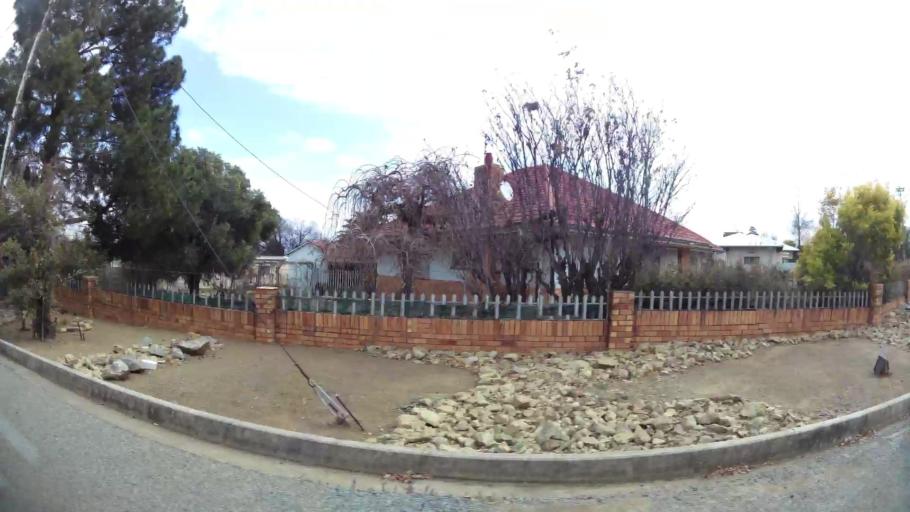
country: ZA
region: Orange Free State
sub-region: Fezile Dabi District Municipality
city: Kroonstad
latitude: -27.6505
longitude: 27.2337
